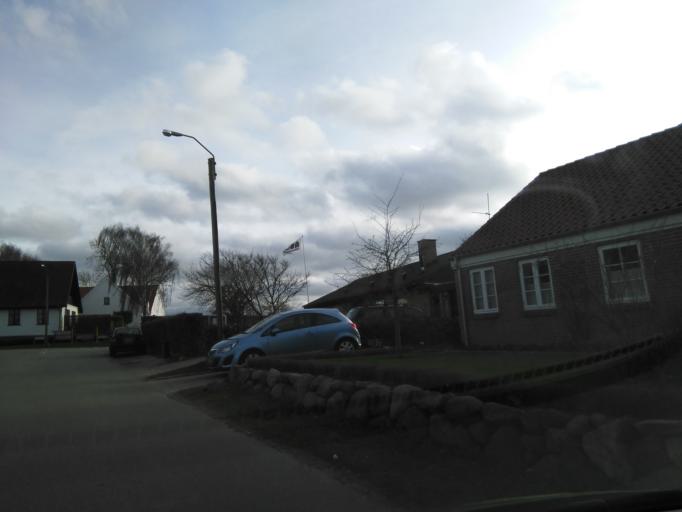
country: DK
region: Central Jutland
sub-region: Arhus Kommune
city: Framlev
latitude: 56.1697
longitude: 10.0417
